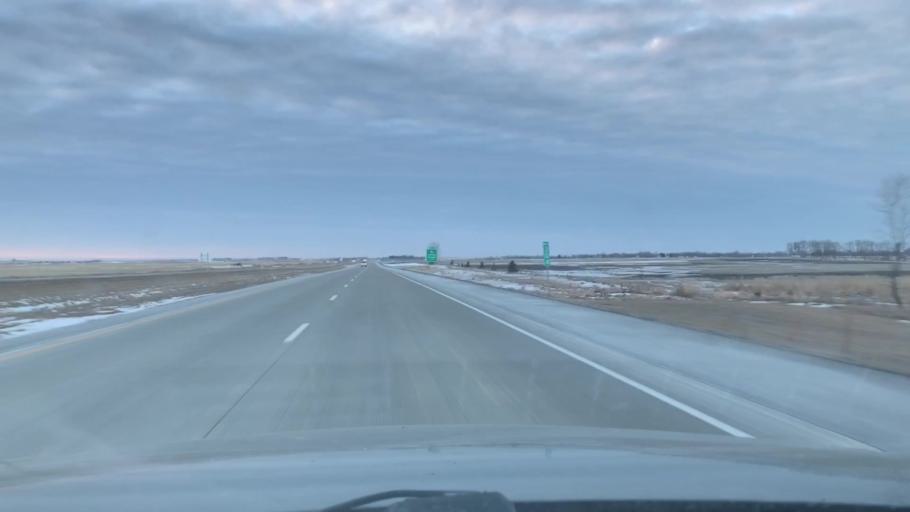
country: US
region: North Dakota
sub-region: Barnes County
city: Valley City
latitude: 46.9201
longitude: -97.7597
